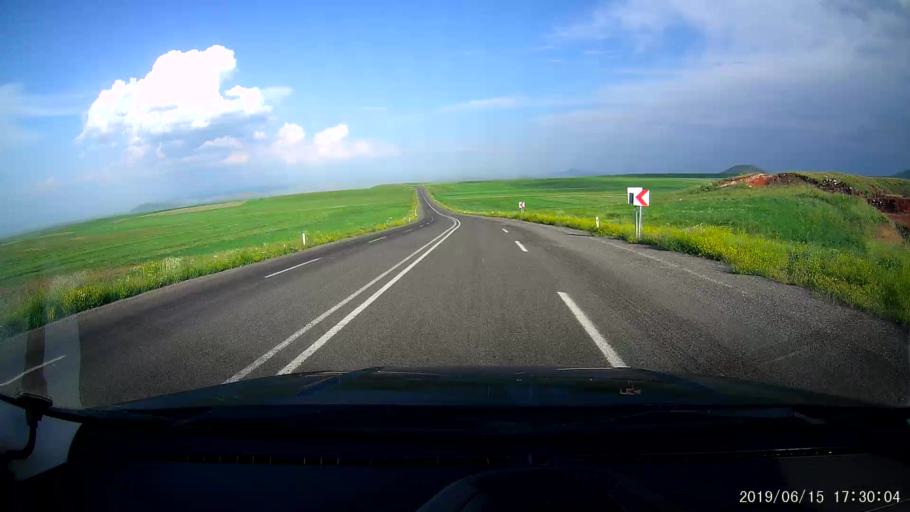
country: TR
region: Kars
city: Basgedikler
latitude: 40.5850
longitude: 43.4625
